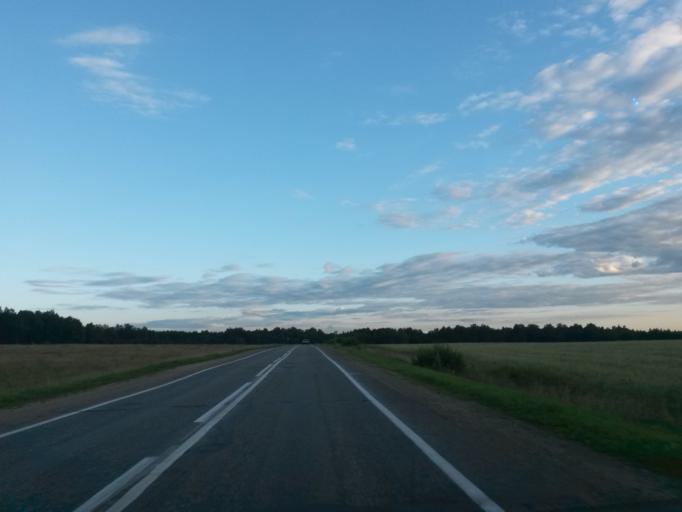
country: RU
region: Jaroslavl
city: Gavrilov-Yam
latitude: 57.4056
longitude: 39.9210
